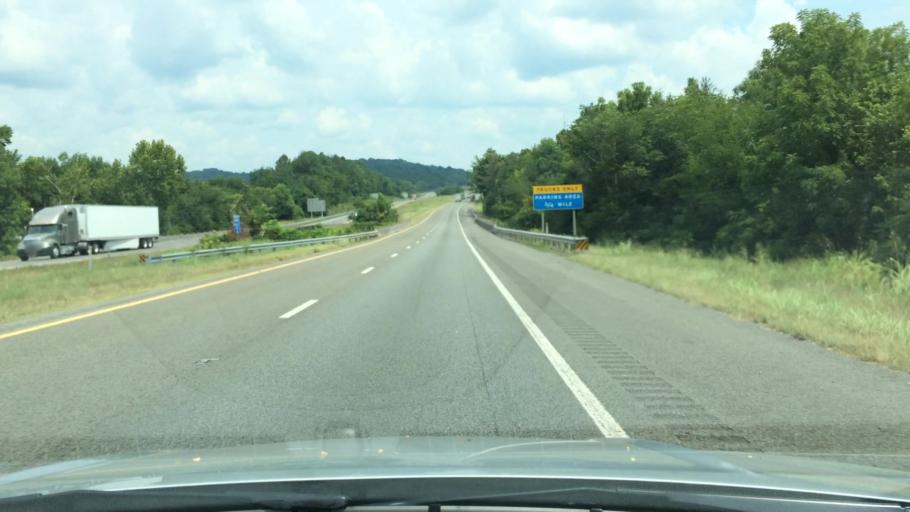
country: US
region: Tennessee
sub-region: Marshall County
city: Cornersville
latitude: 35.3167
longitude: -86.8820
